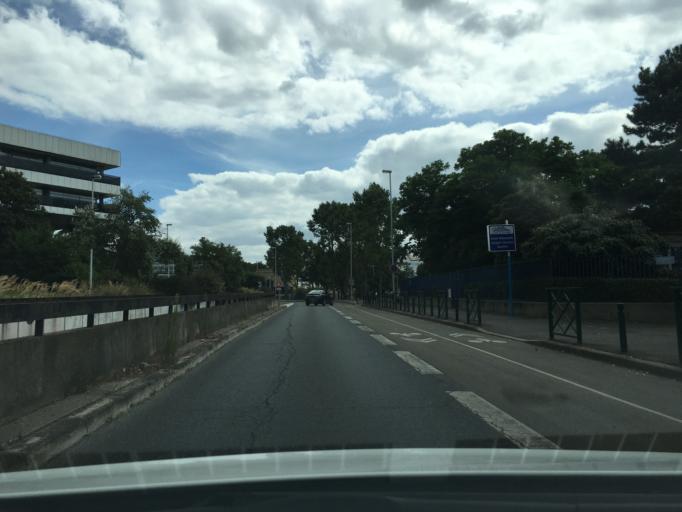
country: FR
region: Ile-de-France
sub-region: Departement des Hauts-de-Seine
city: Nanterre
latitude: 48.8977
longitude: 2.2139
